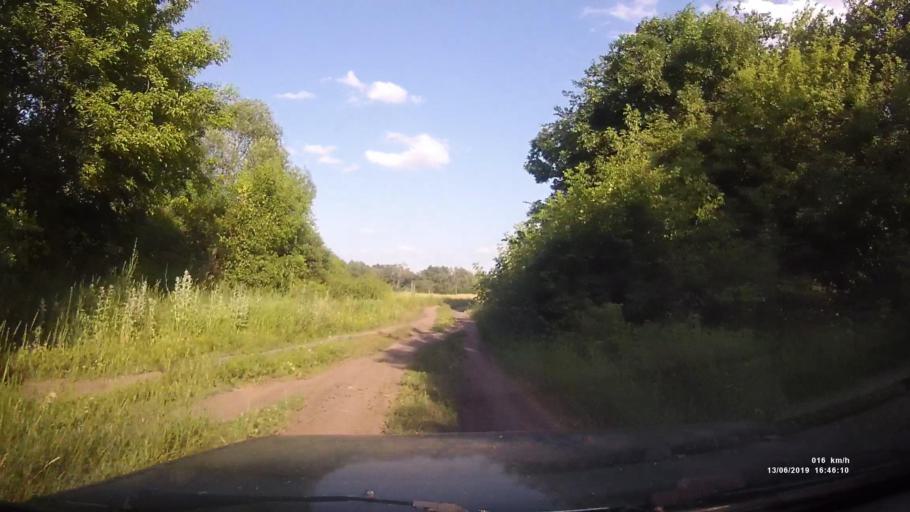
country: RU
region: Rostov
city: Kazanskaya
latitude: 49.9462
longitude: 41.4260
